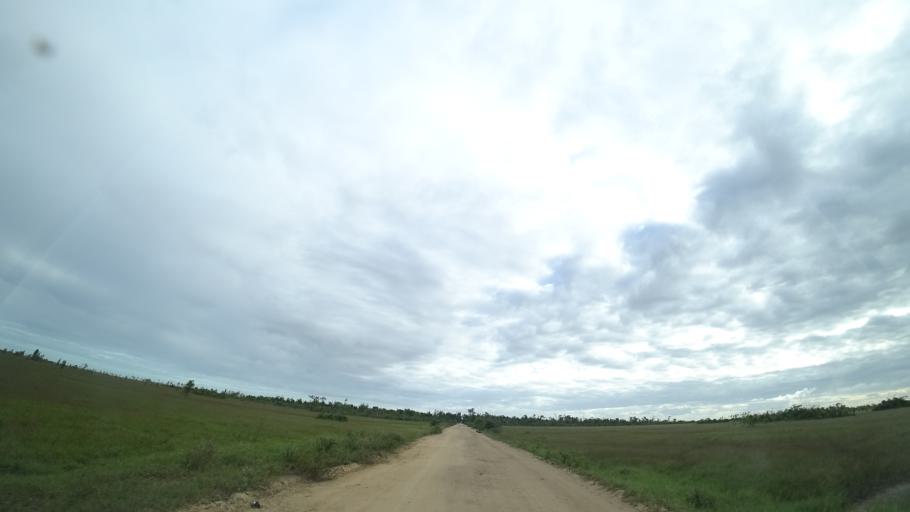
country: MZ
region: Sofala
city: Beira
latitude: -19.7352
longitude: 34.9732
